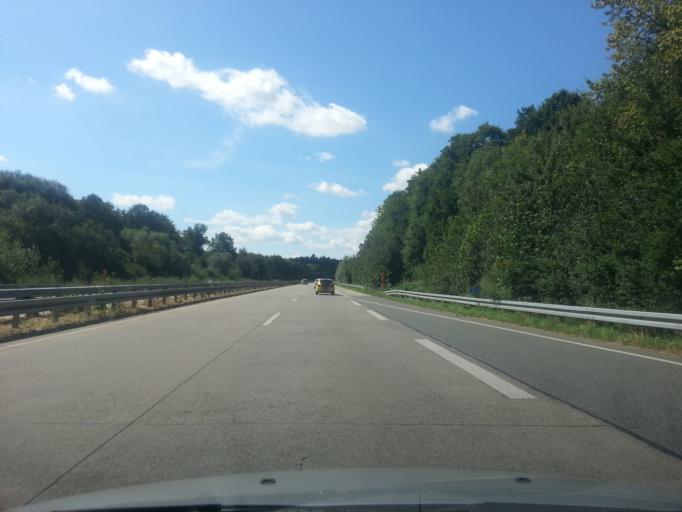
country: DE
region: Hesse
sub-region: Regierungsbezirk Darmstadt
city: Munster
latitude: 49.9034
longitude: 8.8682
